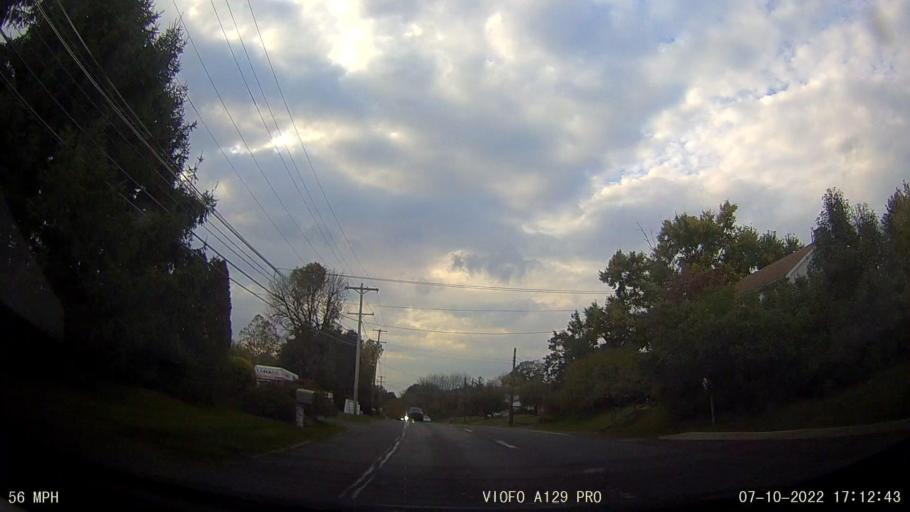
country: US
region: Pennsylvania
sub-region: Berks County
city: Amity Gardens
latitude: 40.2616
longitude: -75.7339
